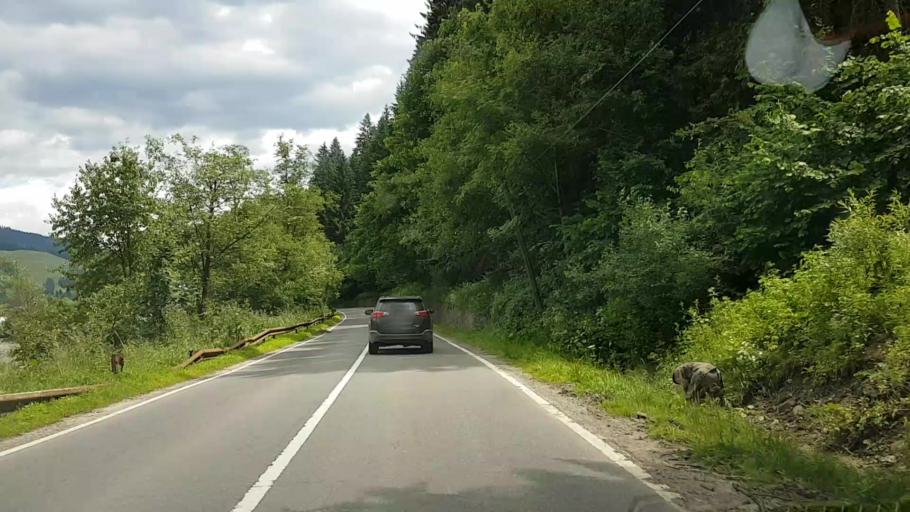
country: RO
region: Neamt
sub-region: Comuna Farcasa
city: Farcasa
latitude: 47.1369
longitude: 25.8645
